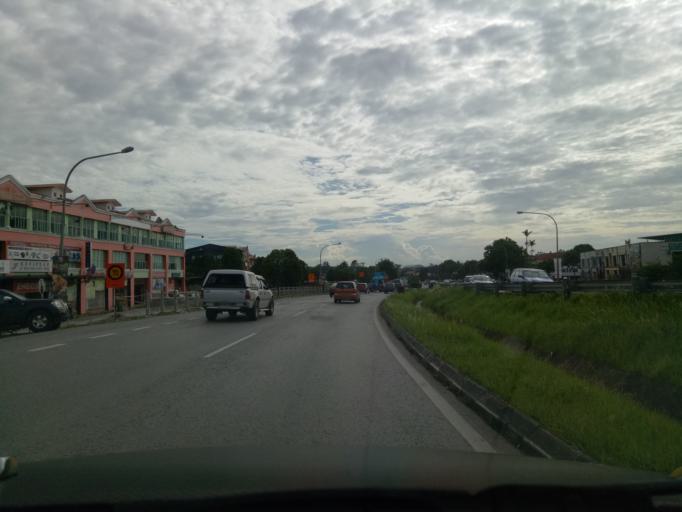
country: MY
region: Sarawak
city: Kuching
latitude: 1.4741
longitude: 110.3289
